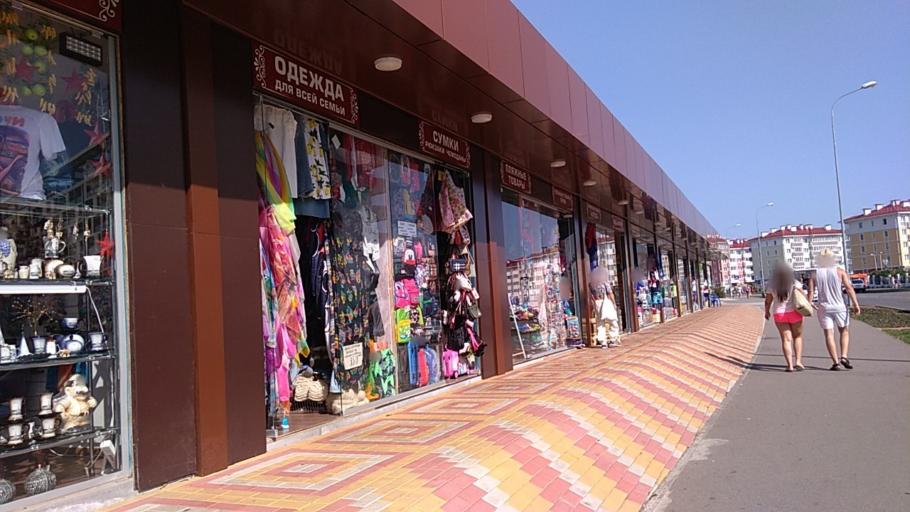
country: RU
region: Krasnodarskiy
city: Adler
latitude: 43.3912
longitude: 39.9886
